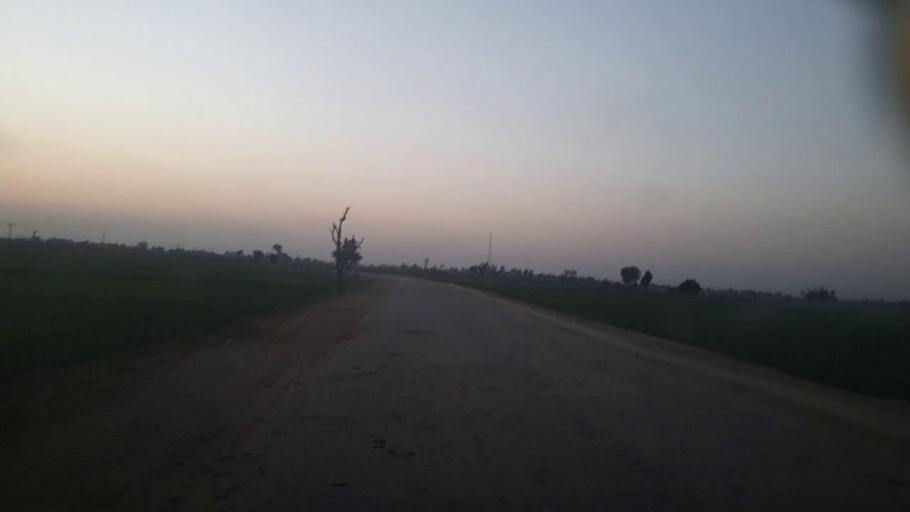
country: PK
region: Sindh
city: Kandiari
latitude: 26.6766
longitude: 68.9518
